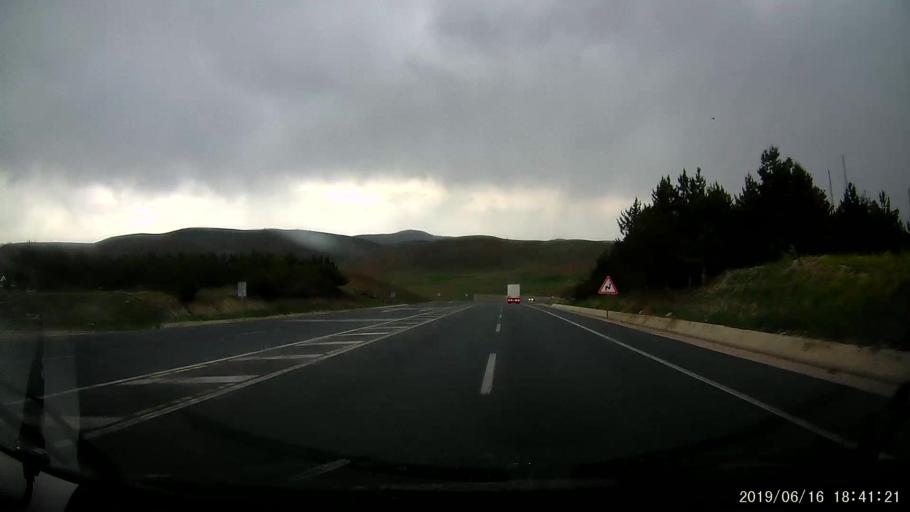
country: TR
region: Erzincan
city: Catalarmut
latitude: 39.8743
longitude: 39.1295
